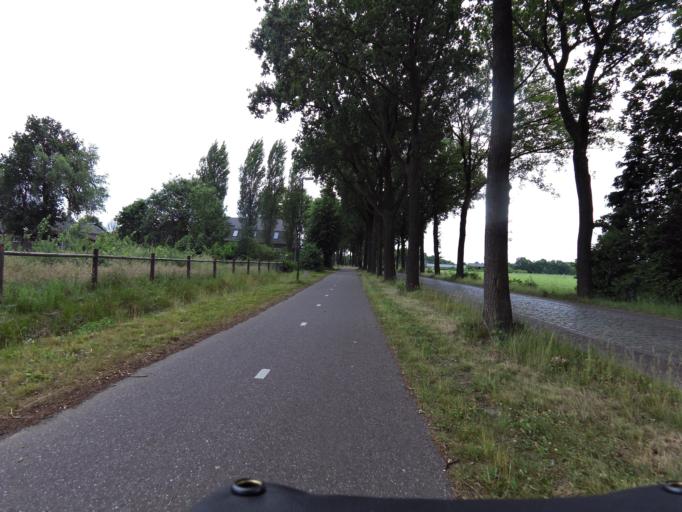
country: NL
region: North Brabant
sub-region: Gemeente Bladel en Netersel
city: Bladel
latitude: 51.3816
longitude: 5.2129
